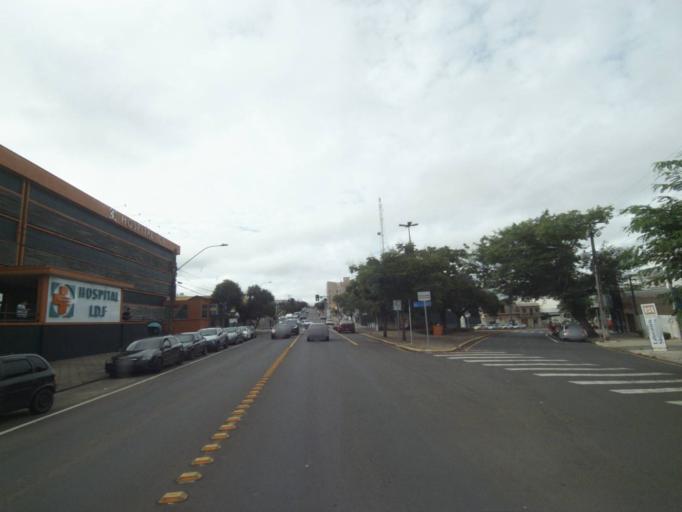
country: BR
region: Parana
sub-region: Telemaco Borba
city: Telemaco Borba
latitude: -24.3256
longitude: -50.6170
